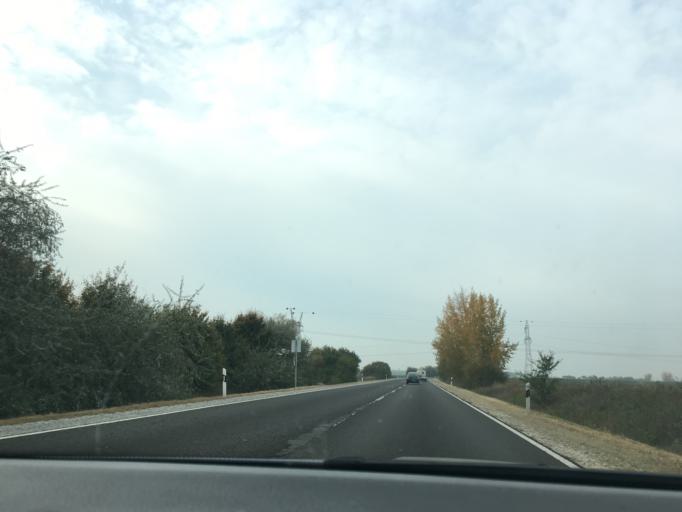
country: HU
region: Jasz-Nagykun-Szolnok
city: Toszeg
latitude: 47.1588
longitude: 20.1137
